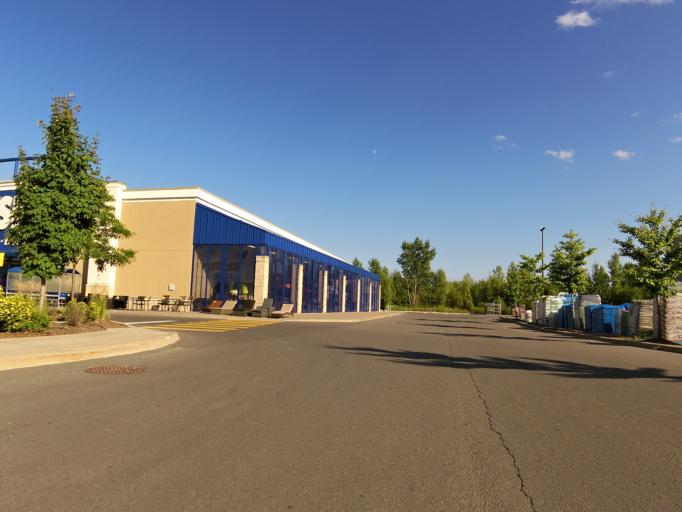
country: CA
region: Ontario
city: Ottawa
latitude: 45.3381
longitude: -75.7128
